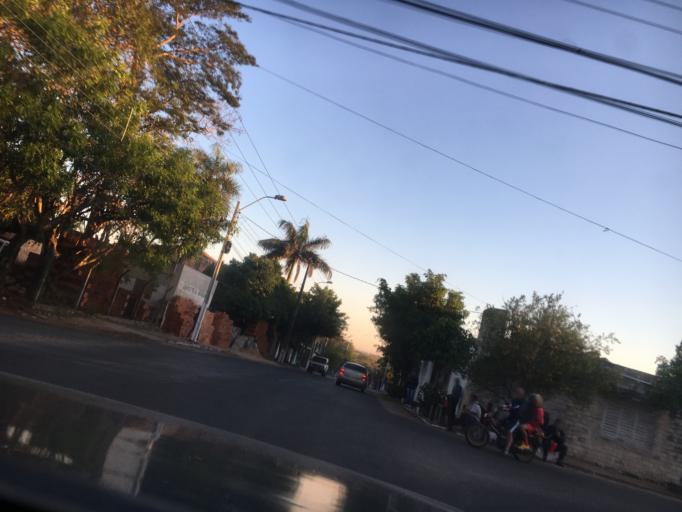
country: PY
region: Central
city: Lambare
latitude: -25.3260
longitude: -57.6108
